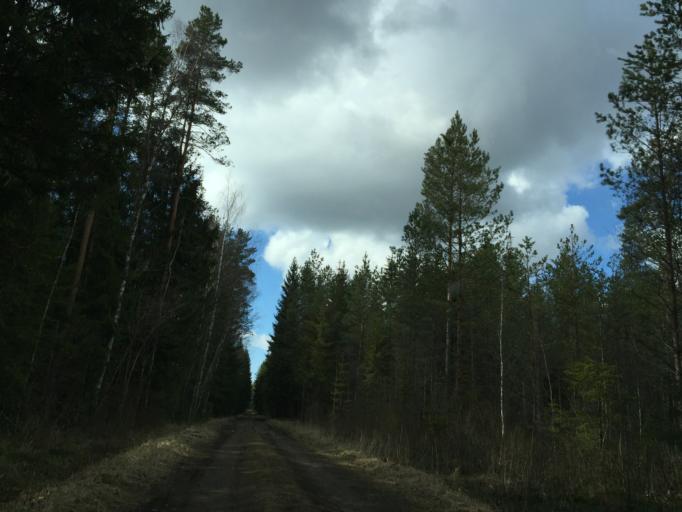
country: LV
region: Garkalne
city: Garkalne
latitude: 56.9490
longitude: 24.4779
